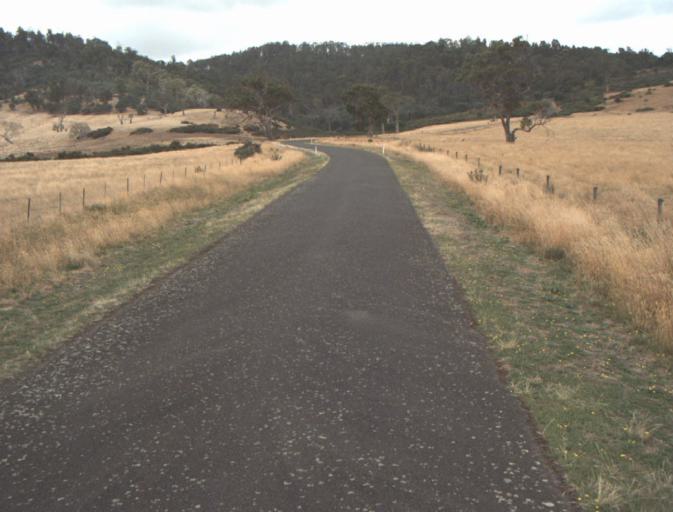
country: AU
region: Tasmania
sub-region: Northern Midlands
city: Evandale
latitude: -41.5062
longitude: 147.4815
